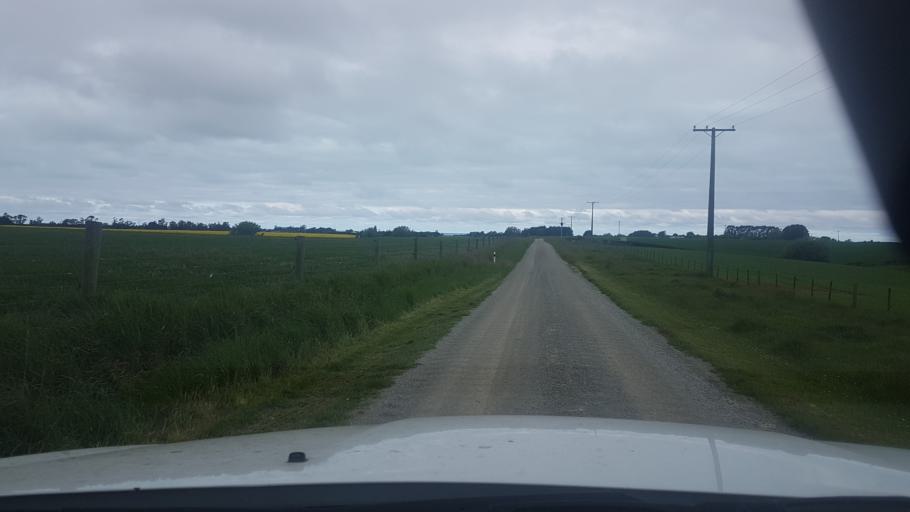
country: NZ
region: Canterbury
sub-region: Timaru District
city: Timaru
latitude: -44.4426
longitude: 171.2014
